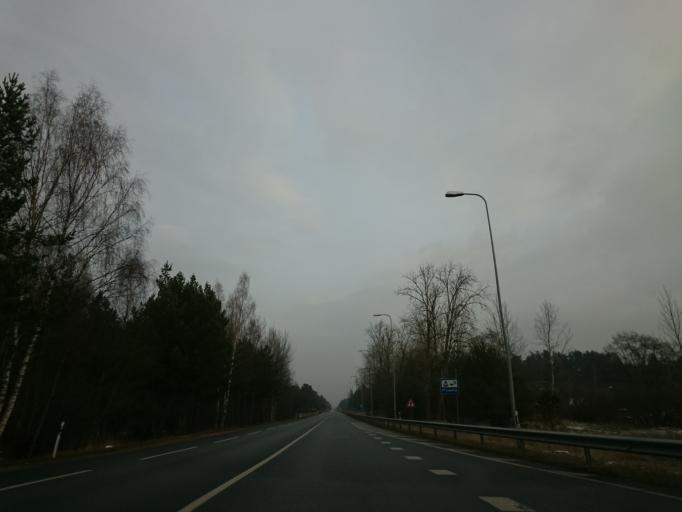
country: LV
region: Adazi
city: Adazi
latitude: 57.1241
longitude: 24.3274
